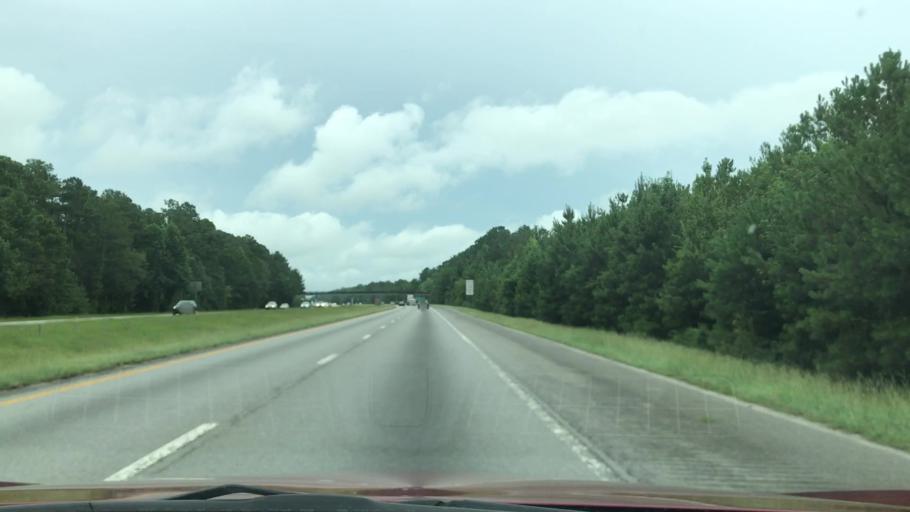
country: US
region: South Carolina
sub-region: Orangeburg County
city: Brookdale
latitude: 33.4530
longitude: -80.7244
